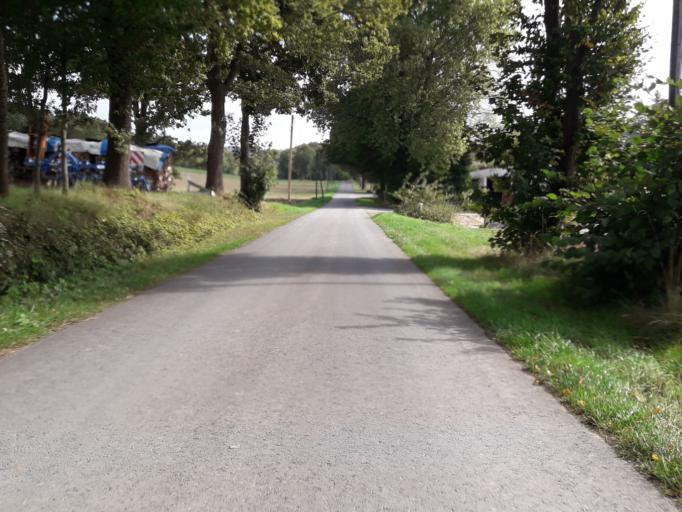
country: DE
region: North Rhine-Westphalia
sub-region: Regierungsbezirk Detmold
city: Altenbeken
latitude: 51.7160
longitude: 8.9144
